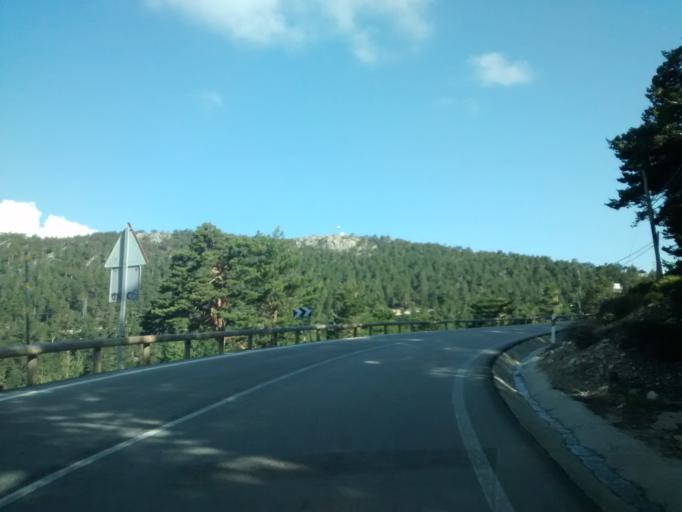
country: ES
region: Madrid
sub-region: Provincia de Madrid
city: Navacerrada
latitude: 40.7817
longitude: -4.0020
